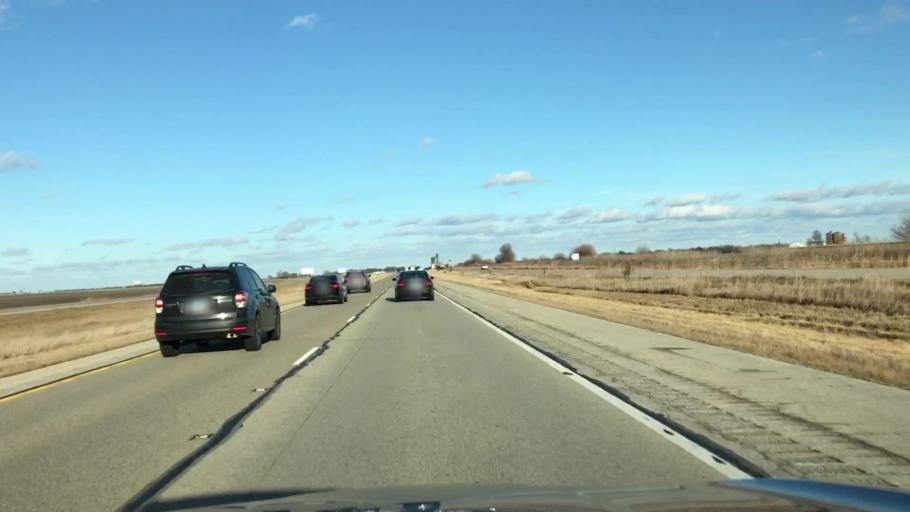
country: US
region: Illinois
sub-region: McLean County
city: Normal
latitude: 40.5493
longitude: -88.9220
